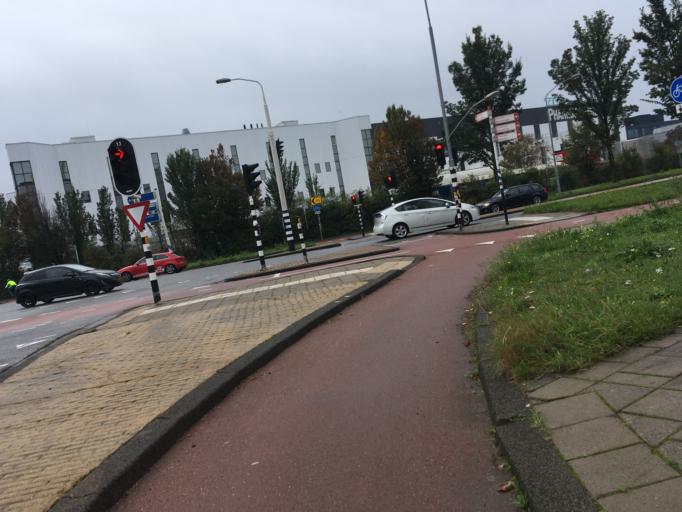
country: NL
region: North Holland
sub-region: Gemeente Haarlem
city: Haarlem
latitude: 52.3880
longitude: 4.6701
